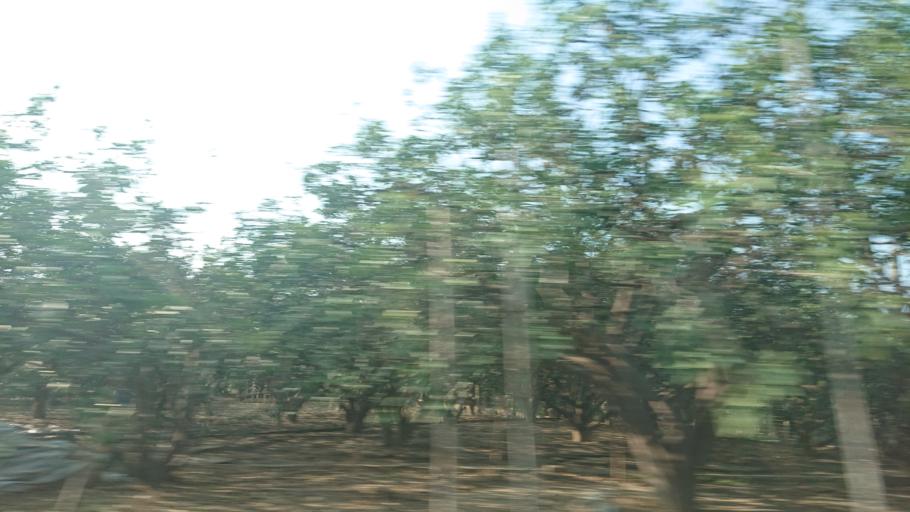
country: TW
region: Taiwan
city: Xinying
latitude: 23.1798
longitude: 120.2641
